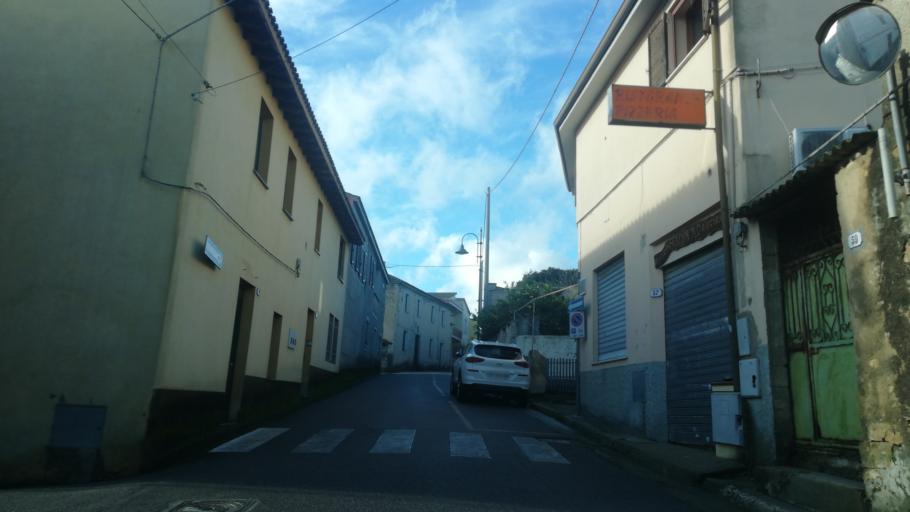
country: IT
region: Sardinia
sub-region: Provincia di Medio Campidano
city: Villanovaforru
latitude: 39.6316
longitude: 8.8719
